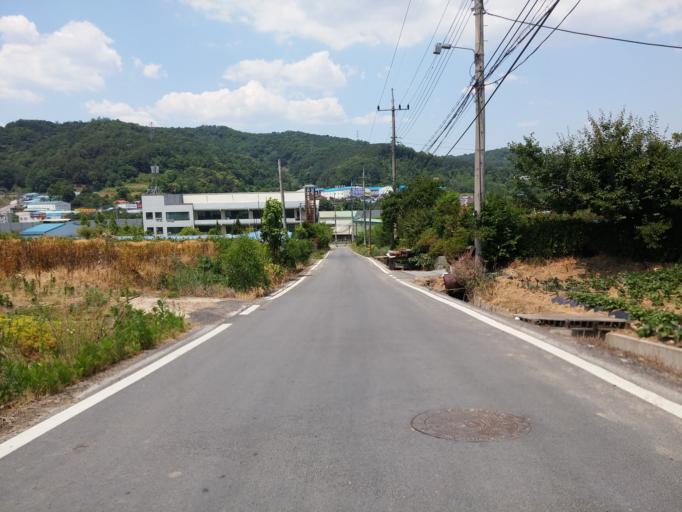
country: KR
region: Chungcheongbuk-do
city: Cheongju-si
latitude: 36.5555
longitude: 127.4356
